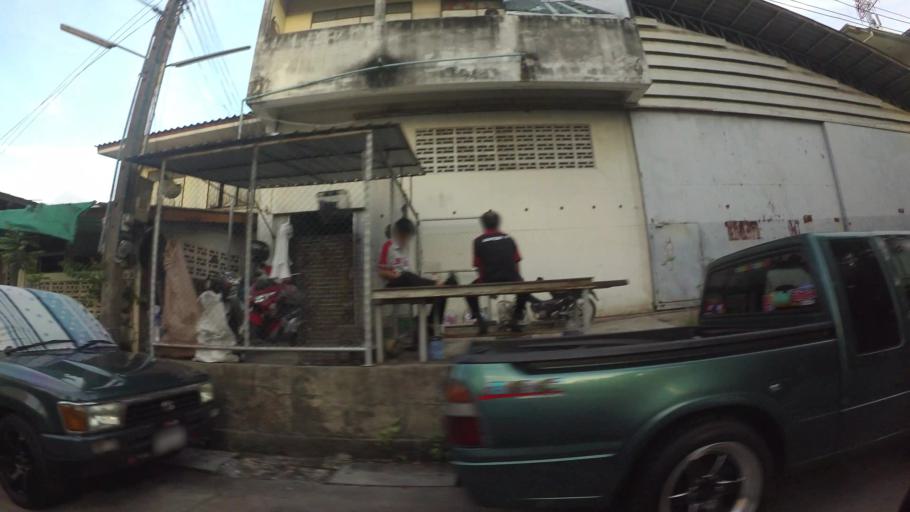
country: TH
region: Rayong
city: Rayong
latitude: 12.6822
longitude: 101.2820
